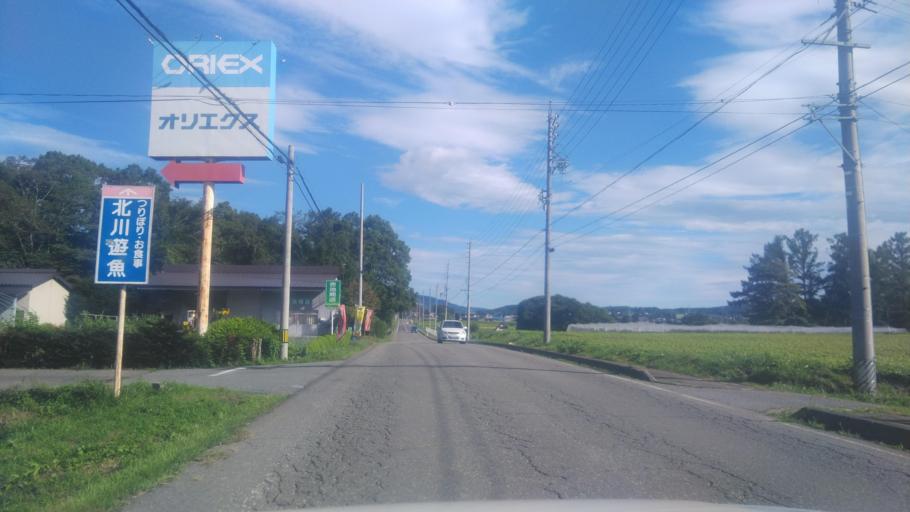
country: JP
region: Nagano
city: Nagano-shi
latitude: 36.7839
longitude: 138.1990
